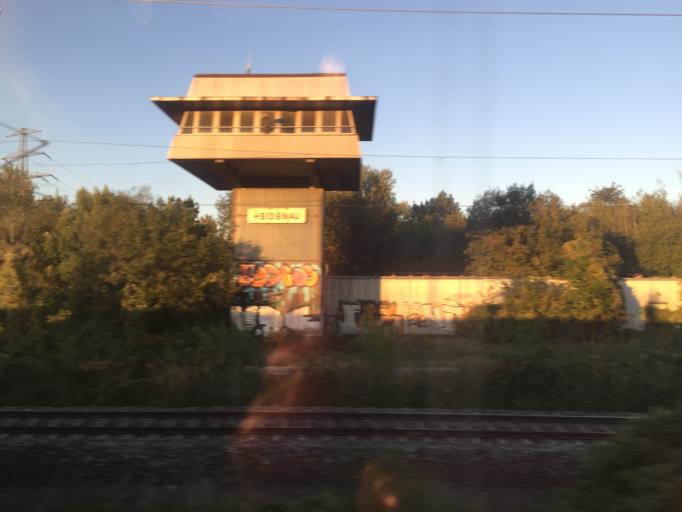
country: DE
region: Saxony
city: Heidenau
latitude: 50.9845
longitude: 13.8534
